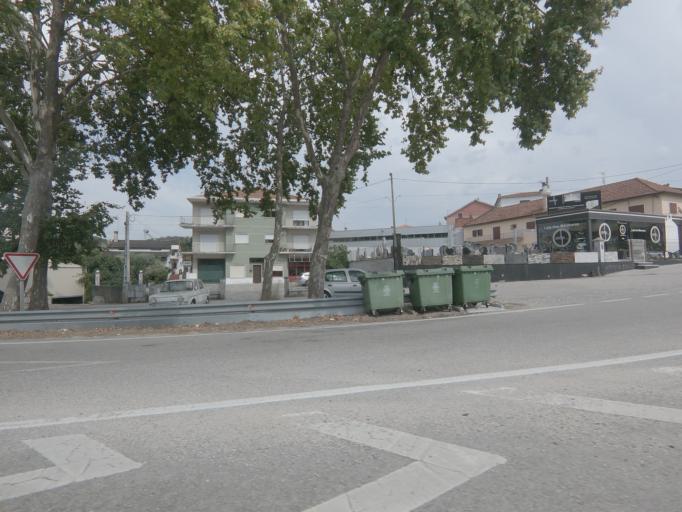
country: PT
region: Leiria
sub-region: Pombal
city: Pombal
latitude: 39.9047
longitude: -8.6339
